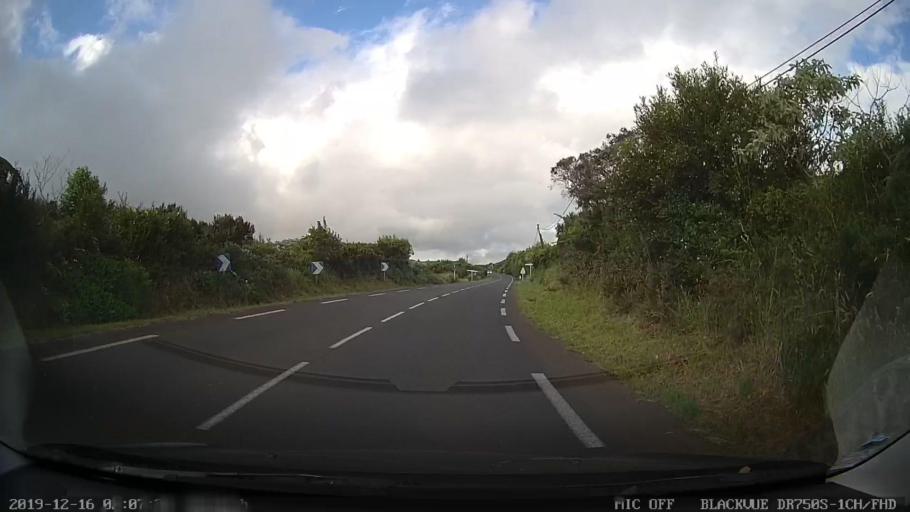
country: RE
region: Reunion
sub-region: Reunion
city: Cilaos
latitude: -21.1786
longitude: 55.5796
